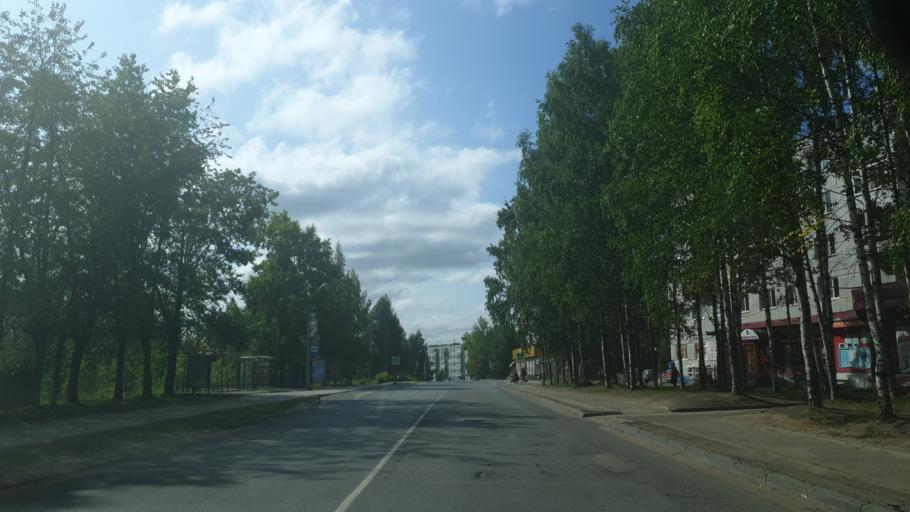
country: RU
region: Komi Republic
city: Ezhva
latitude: 61.7927
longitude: 50.7504
